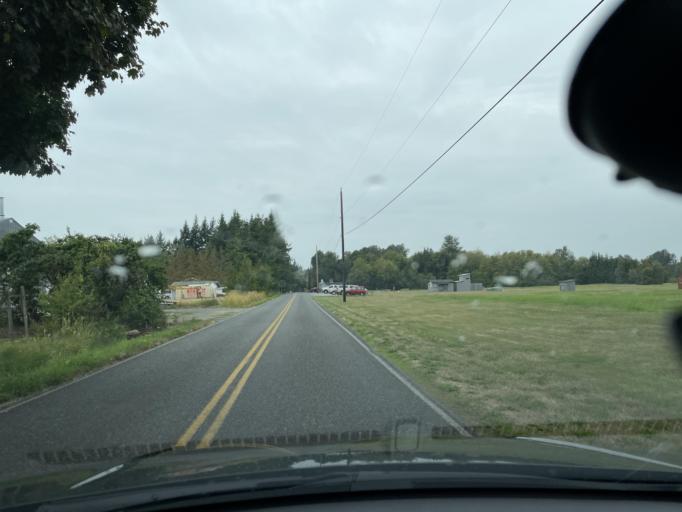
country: US
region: Washington
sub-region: Whatcom County
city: Marietta-Alderwood
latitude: 48.8261
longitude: -122.5300
